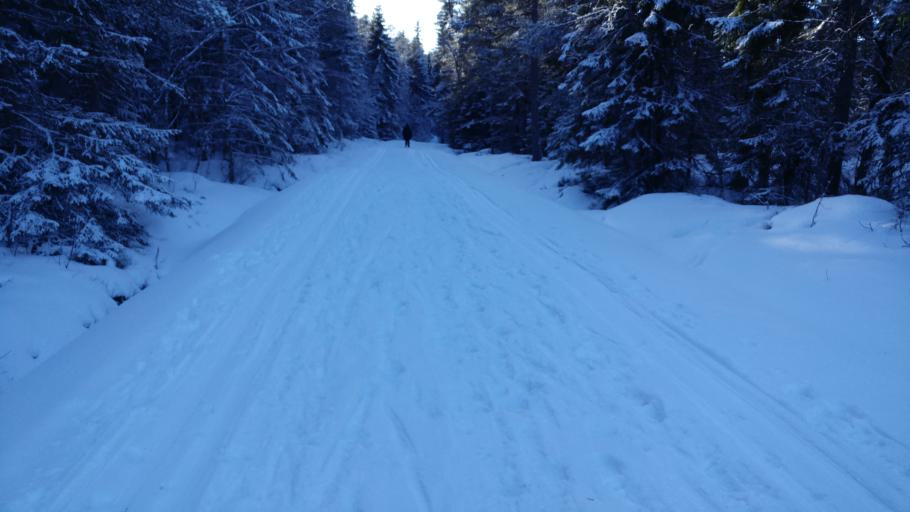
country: NO
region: Sor-Trondelag
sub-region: Trondheim
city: Trondheim
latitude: 63.4368
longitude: 10.2970
